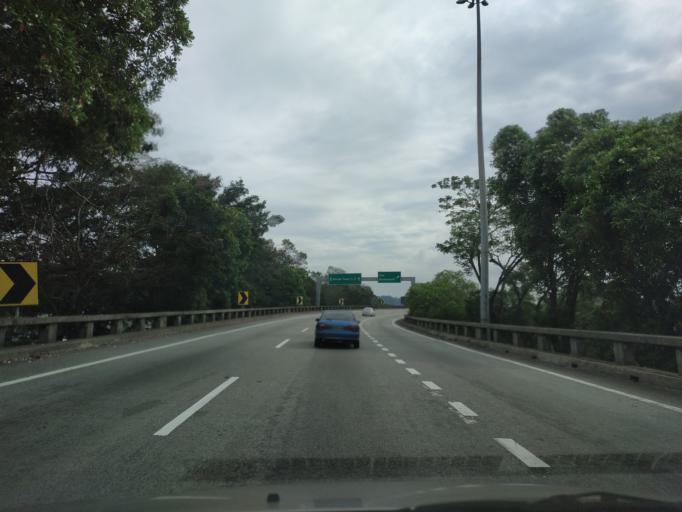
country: MY
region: Penang
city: Perai
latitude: 5.3663
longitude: 100.4000
